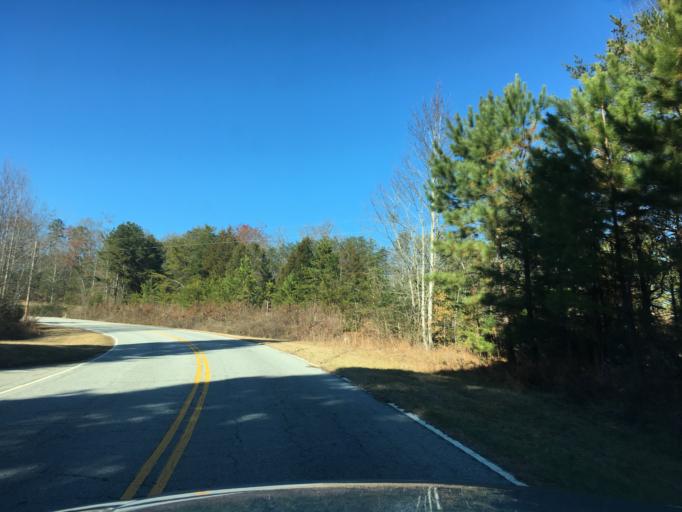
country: US
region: South Carolina
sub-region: Oconee County
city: Walhalla
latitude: 34.9321
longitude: -82.9896
